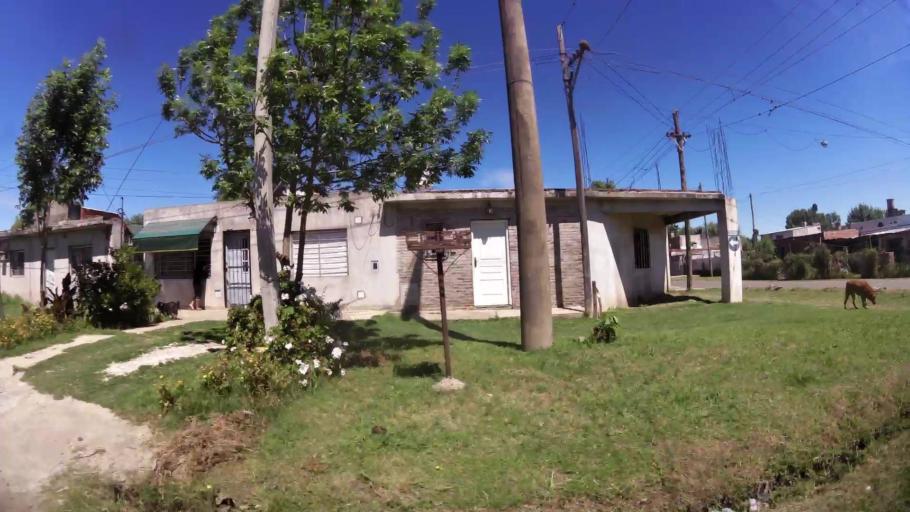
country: AR
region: Santa Fe
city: Perez
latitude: -32.9572
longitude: -60.7153
